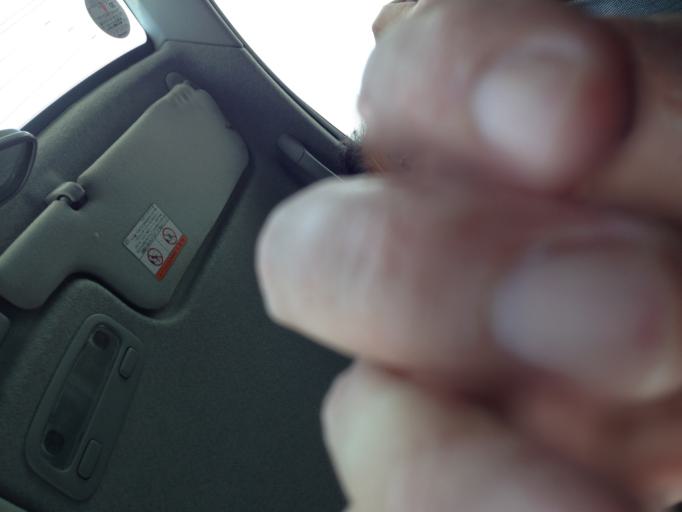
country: JP
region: Shizuoka
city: Hamakita
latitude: 34.8100
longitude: 137.7963
